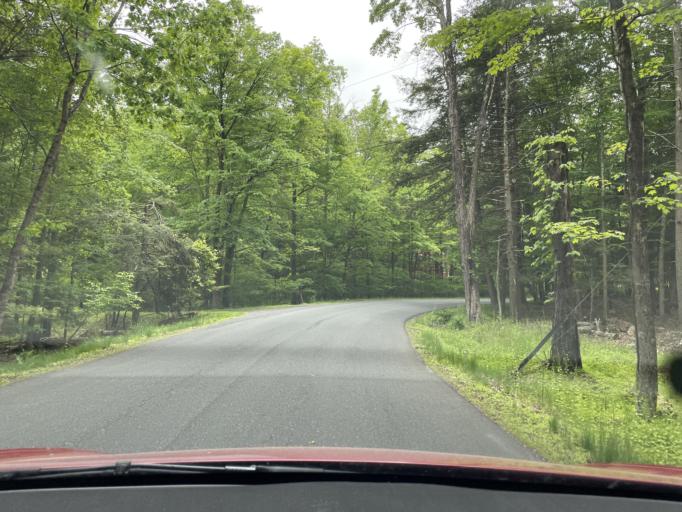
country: US
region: New York
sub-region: Ulster County
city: Zena
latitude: 41.9969
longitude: -74.0567
